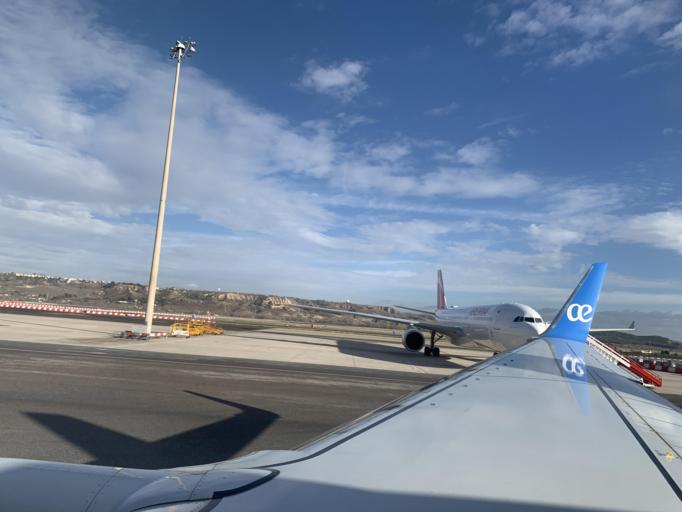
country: ES
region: Madrid
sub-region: Provincia de Madrid
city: Barajas de Madrid
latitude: 40.4916
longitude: -3.5645
